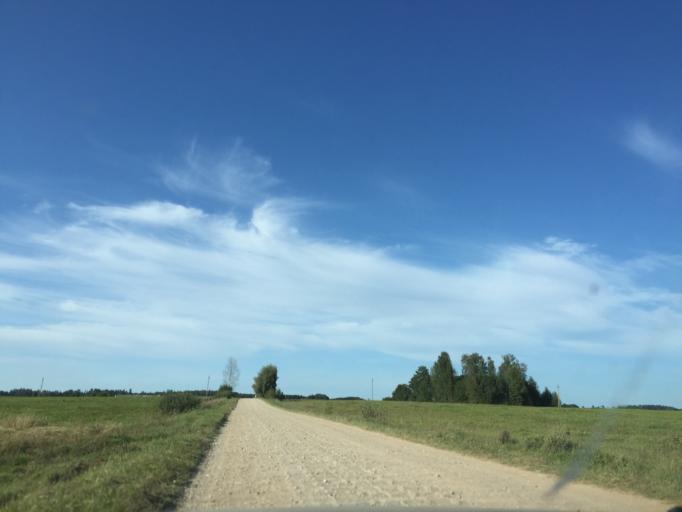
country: LT
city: Zarasai
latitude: 55.8031
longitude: 25.9481
